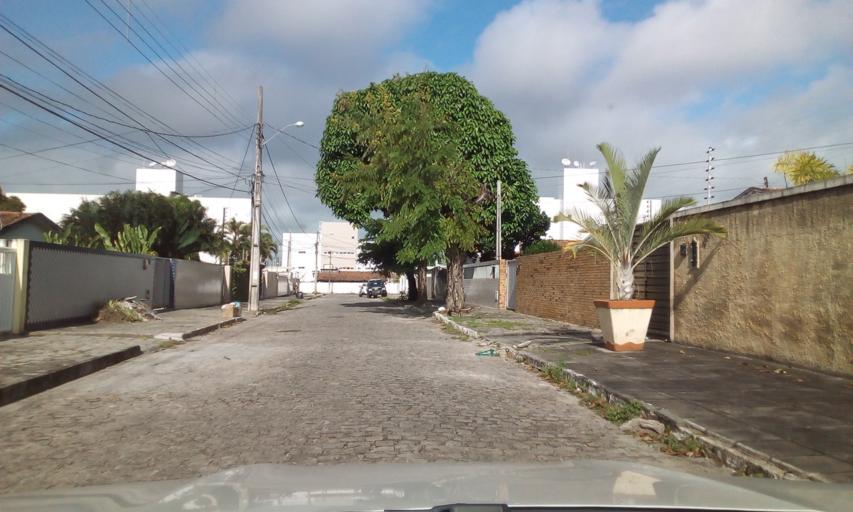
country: BR
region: Paraiba
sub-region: Joao Pessoa
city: Joao Pessoa
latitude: -7.1435
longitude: -34.8417
